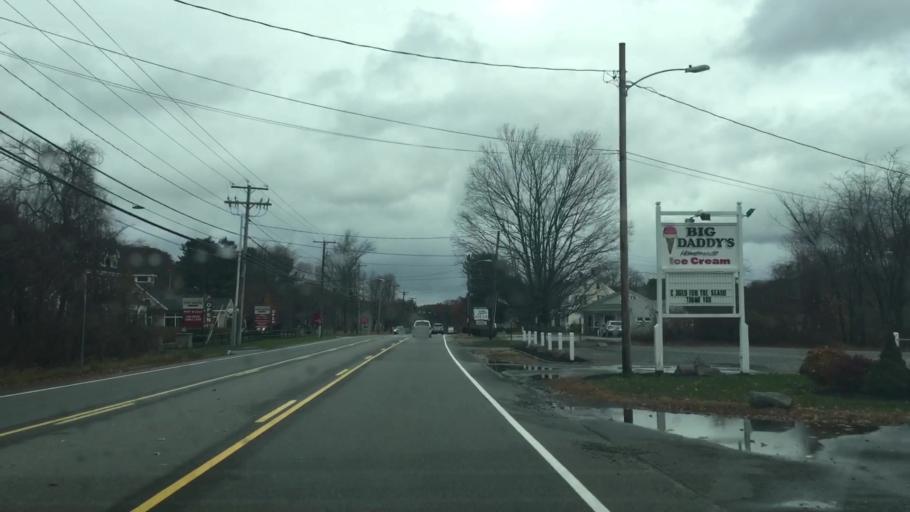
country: US
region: Maine
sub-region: York County
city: Wells Beach Station
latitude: 43.3394
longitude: -70.5660
